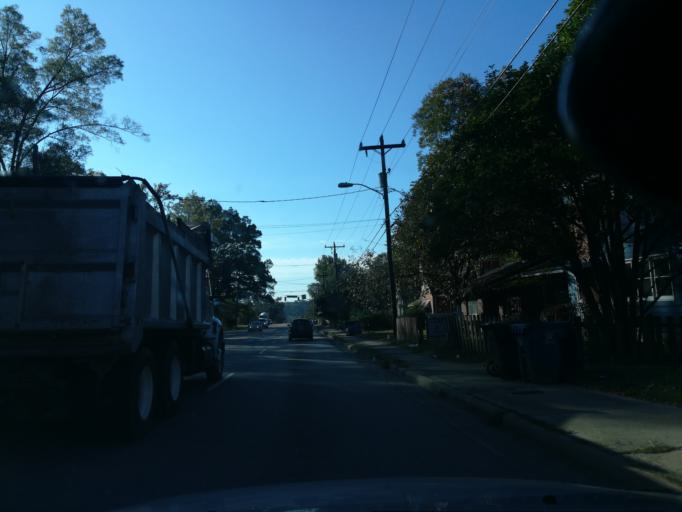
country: US
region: North Carolina
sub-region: Durham County
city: Durham
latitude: 36.0243
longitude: -78.8899
